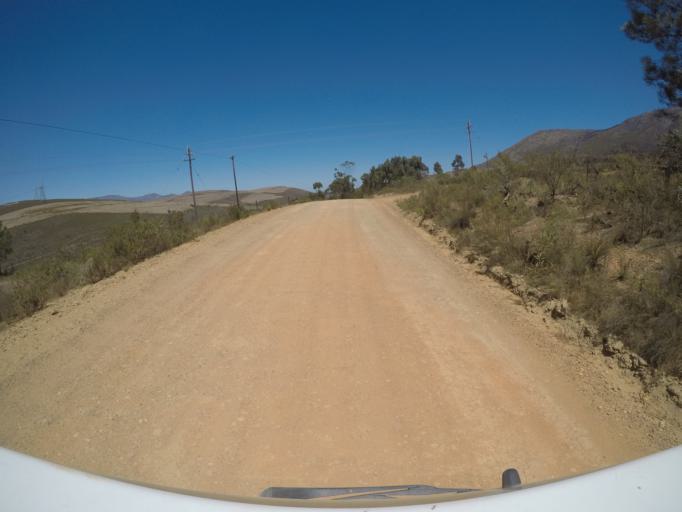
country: ZA
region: Western Cape
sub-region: Overberg District Municipality
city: Caledon
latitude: -34.1970
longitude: 19.2221
